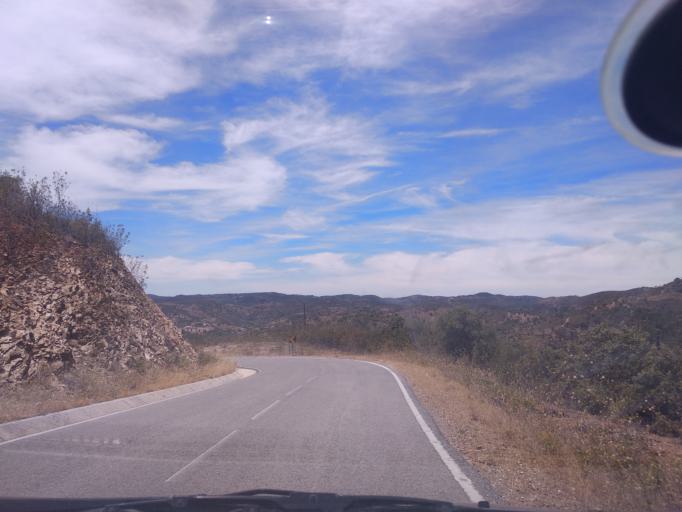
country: PT
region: Faro
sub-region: Sao Bras de Alportel
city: Sao Bras de Alportel
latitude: 37.1874
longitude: -7.7975
